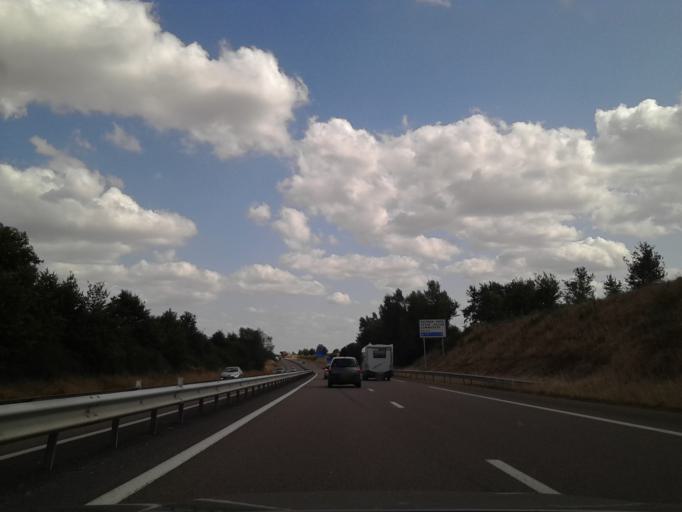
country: FR
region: Auvergne
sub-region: Departement de l'Allier
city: Estivareilles
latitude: 46.4212
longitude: 2.7021
